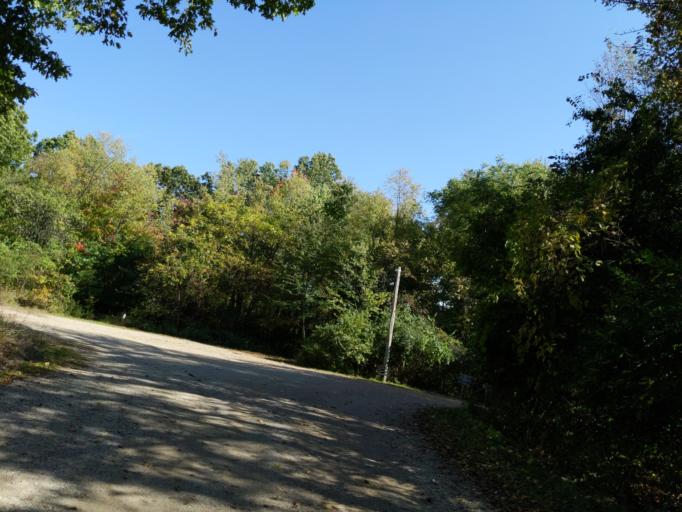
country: US
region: Michigan
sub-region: Clinton County
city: Bath
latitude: 42.8057
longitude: -84.4364
